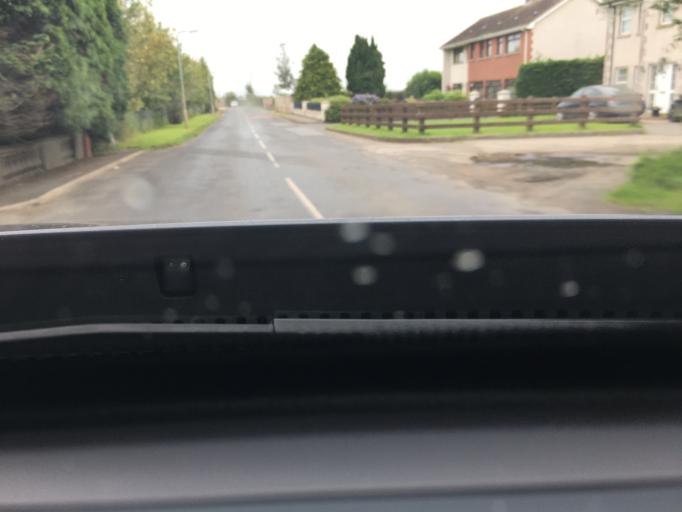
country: GB
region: Northern Ireland
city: Coalisland
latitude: 54.5387
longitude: -6.6218
